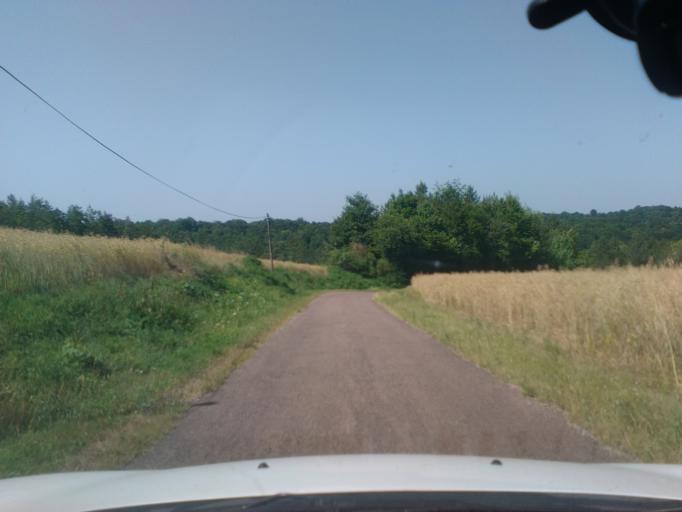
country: FR
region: Lorraine
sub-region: Departement des Vosges
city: Liffol-le-Grand
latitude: 48.3060
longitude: 5.4014
